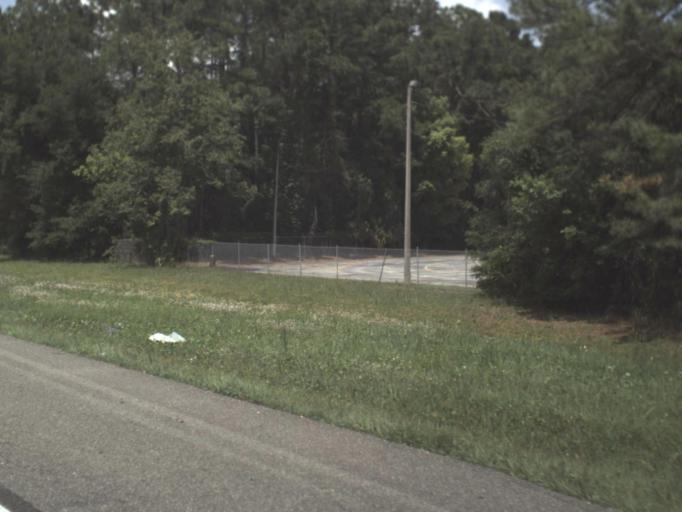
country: US
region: Florida
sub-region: Clay County
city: Bellair-Meadowbrook Terrace
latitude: 30.2924
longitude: -81.7710
